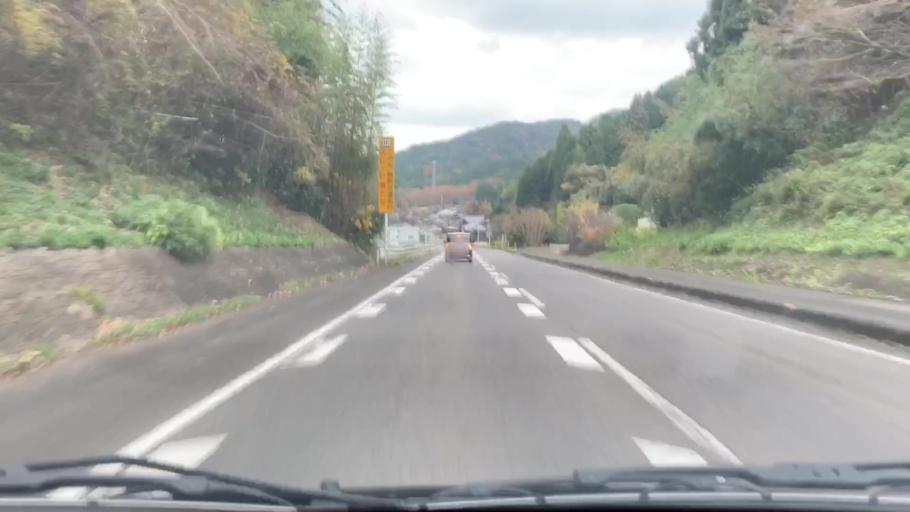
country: JP
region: Saga Prefecture
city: Kashima
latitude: 33.0986
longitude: 130.0475
